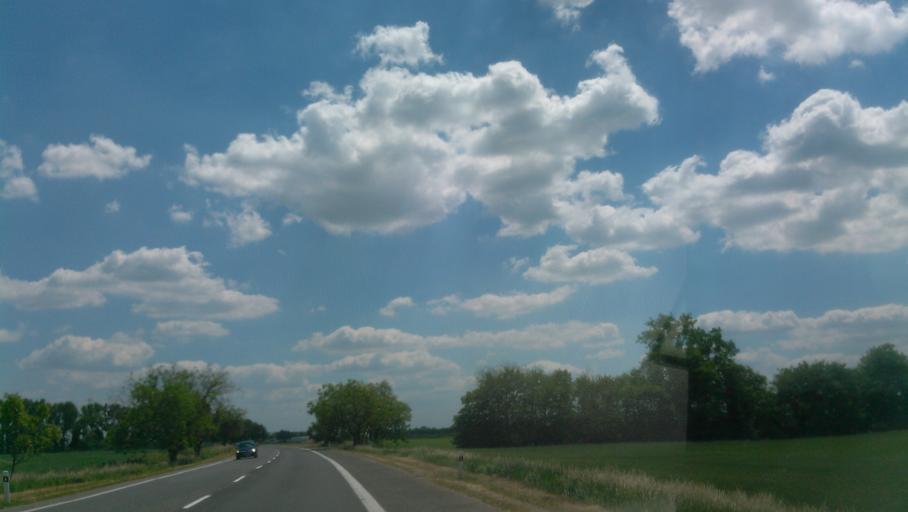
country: SK
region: Bratislavsky
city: Dunajska Luzna
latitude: 48.0595
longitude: 17.2833
